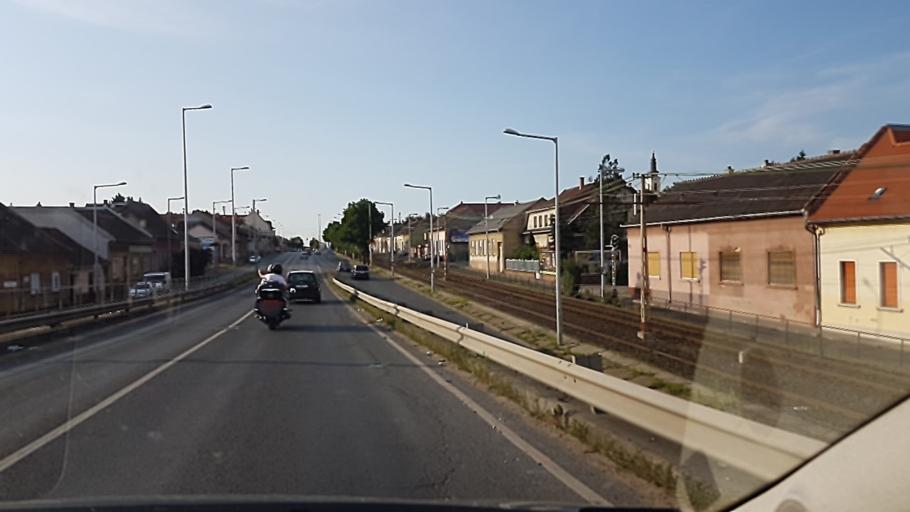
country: HU
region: Budapest
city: Budapest XXIII. keruelet
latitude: 47.3960
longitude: 19.1157
